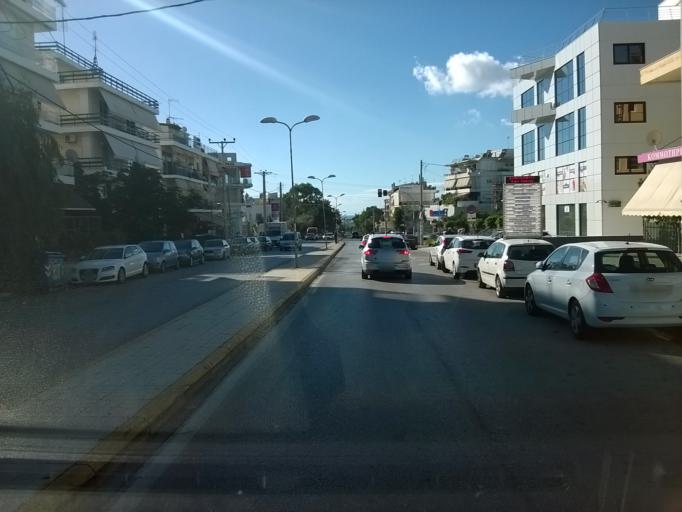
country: GR
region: Attica
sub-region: Nomarchia Athinas
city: Glyfada
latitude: 37.8803
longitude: 23.7585
